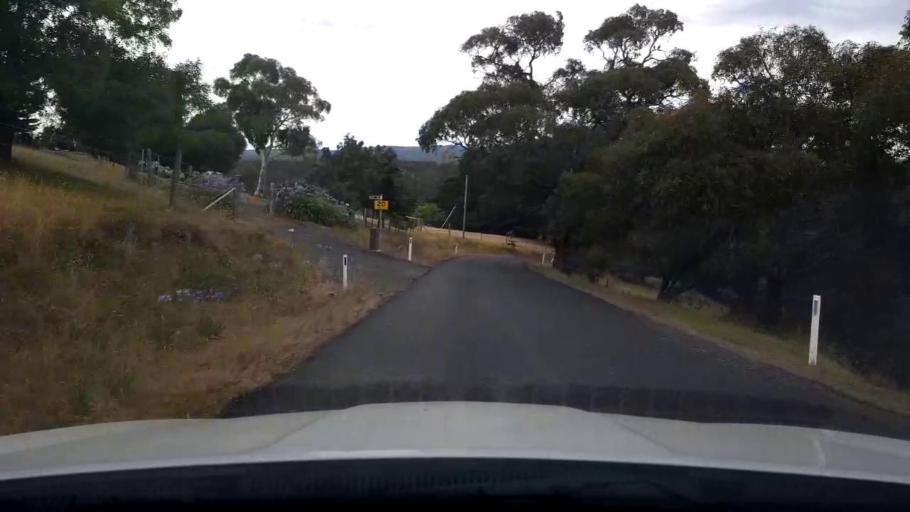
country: AU
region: Victoria
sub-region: Whittlesea
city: Whittlesea
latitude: -37.4903
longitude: 145.0543
